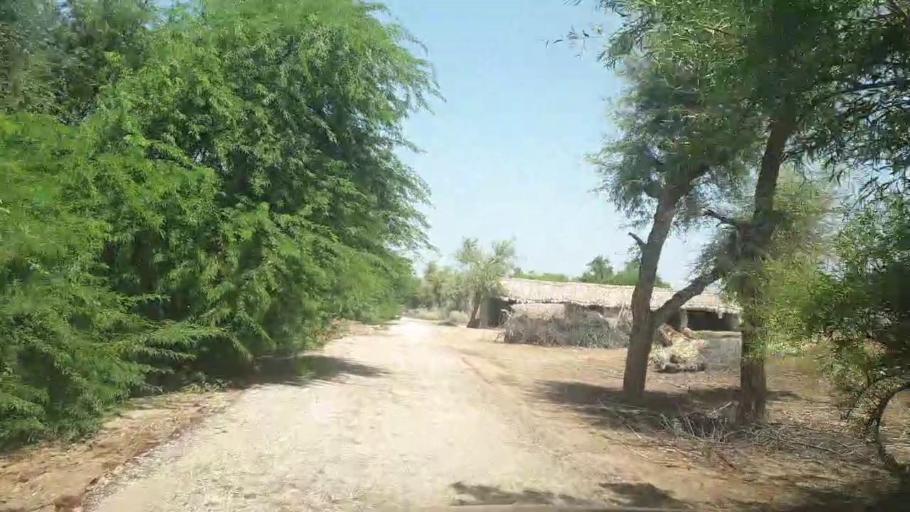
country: PK
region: Sindh
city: Kot Diji
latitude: 27.3180
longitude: 69.0611
